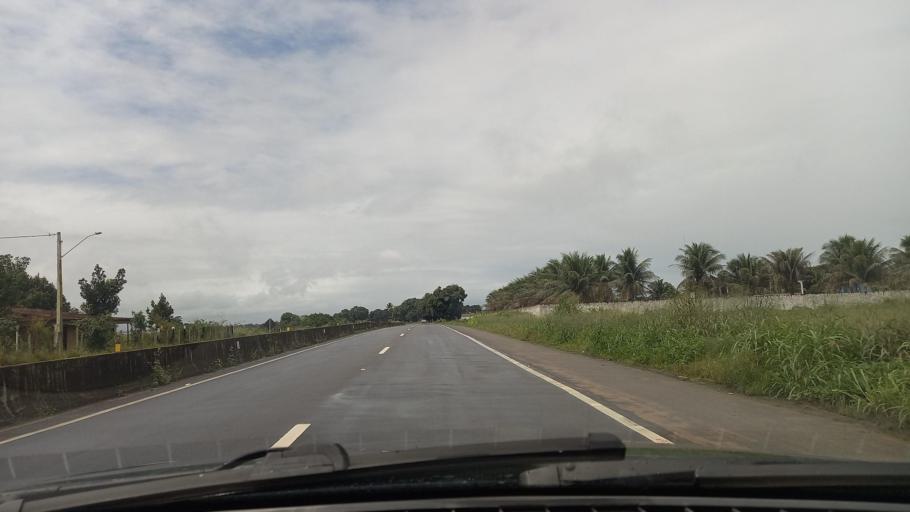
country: BR
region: Alagoas
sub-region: Campo Alegre
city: Campo Alegre
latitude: -9.8030
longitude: -36.2729
